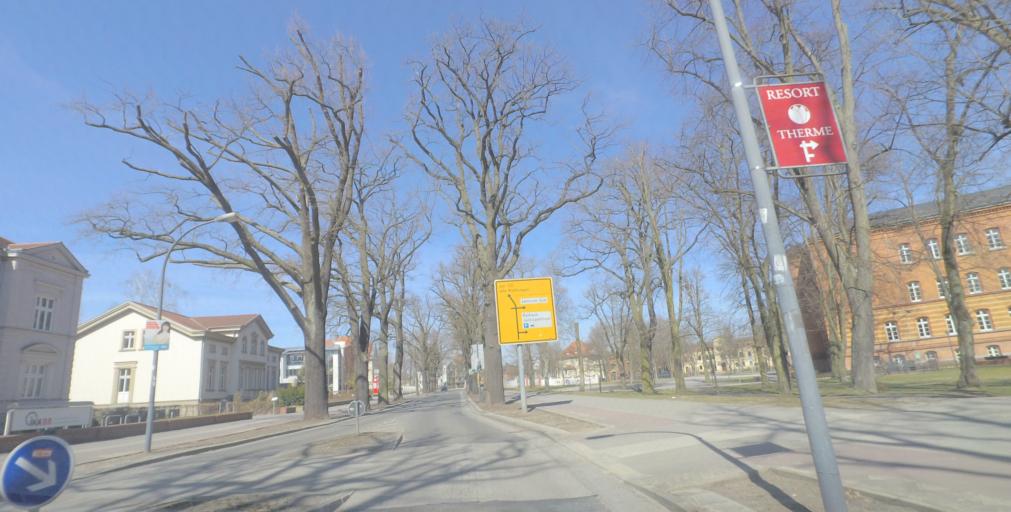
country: DE
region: Brandenburg
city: Neuruppin
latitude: 52.9195
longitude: 12.8006
